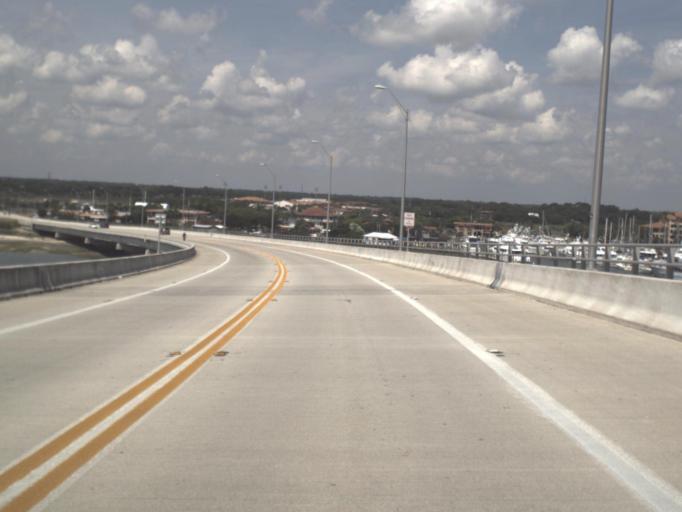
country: US
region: Florida
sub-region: Saint Johns County
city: Villano Beach
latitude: 29.9175
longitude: -81.3031
